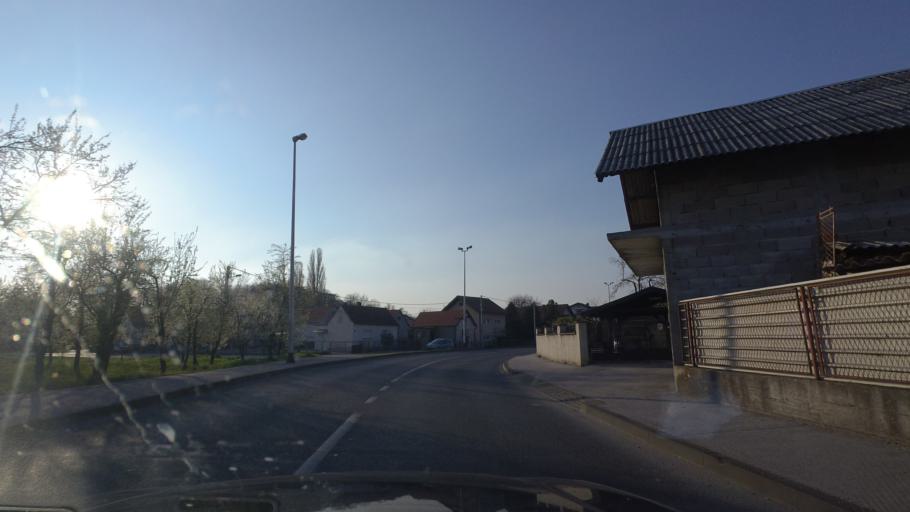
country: HR
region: Grad Zagreb
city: Dubrava
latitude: 45.8160
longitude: 16.0655
